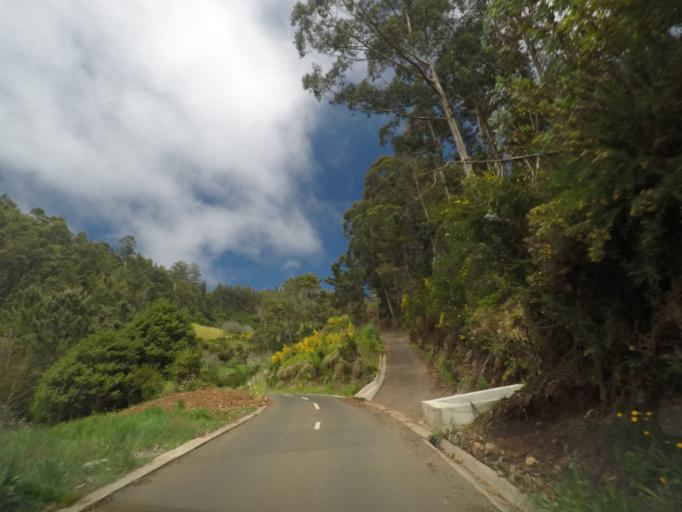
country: PT
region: Madeira
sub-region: Calheta
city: Arco da Calheta
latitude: 32.7239
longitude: -17.1180
